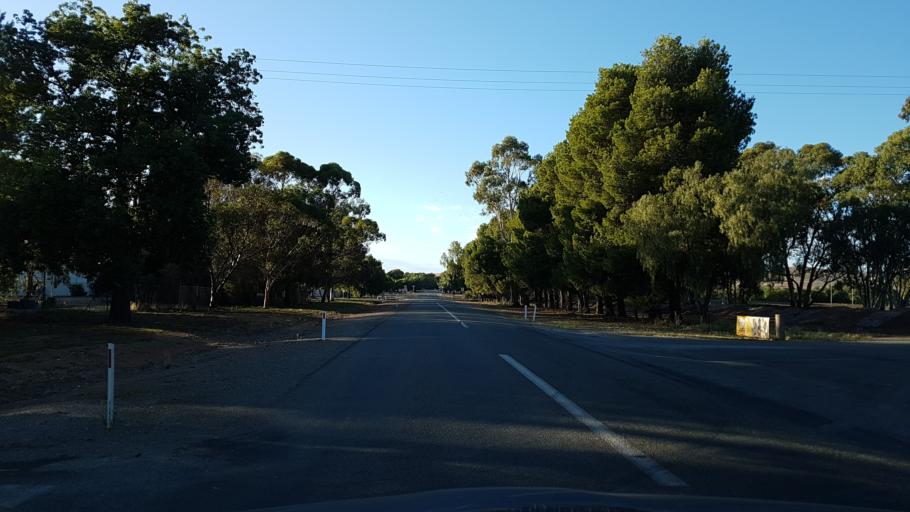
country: AU
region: South Australia
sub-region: Port Pirie City and Dists
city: Crystal Brook
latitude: -33.2737
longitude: 138.3546
